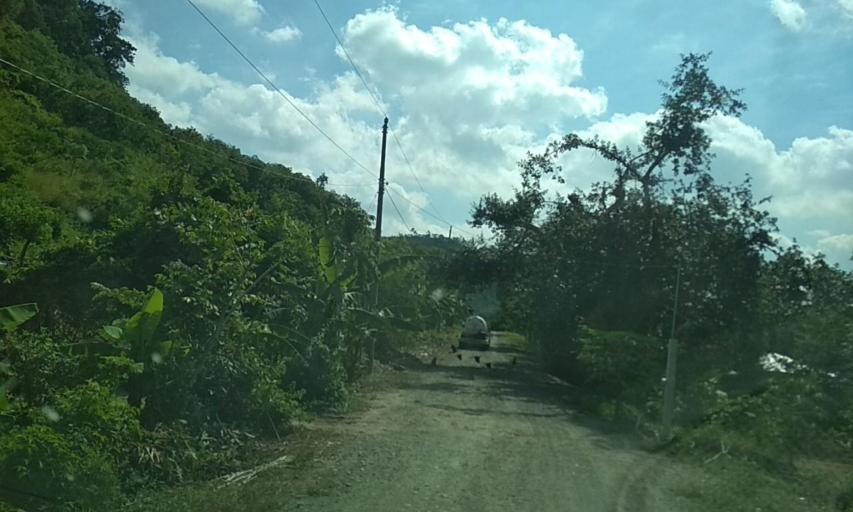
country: MX
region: Veracruz
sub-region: Cazones de Herrera
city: Rancho Nuevo
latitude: 20.6331
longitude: -97.2170
